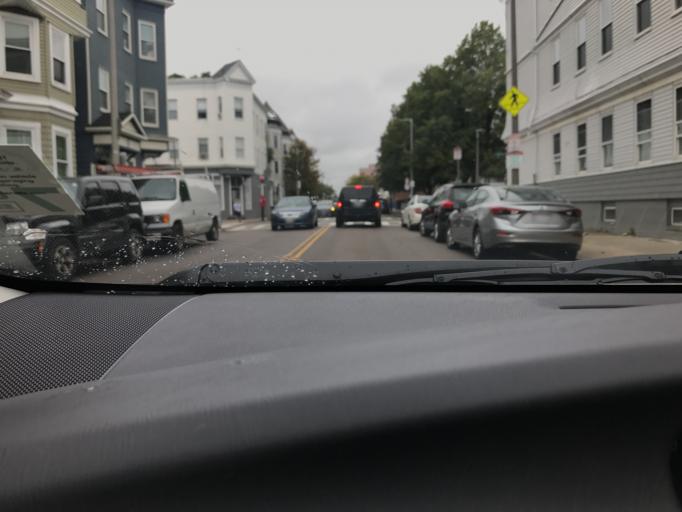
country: US
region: Massachusetts
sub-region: Suffolk County
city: South Boston
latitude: 42.3327
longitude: -71.0353
